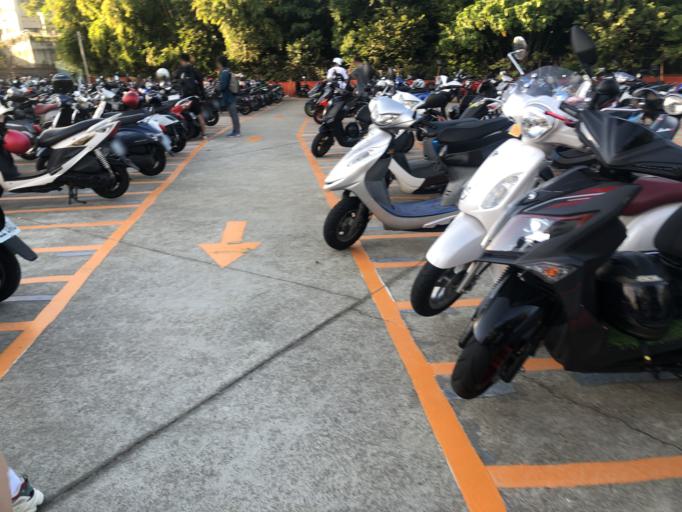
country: TW
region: Taiwan
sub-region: Changhua
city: Chang-hua
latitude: 24.1351
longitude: 120.6019
